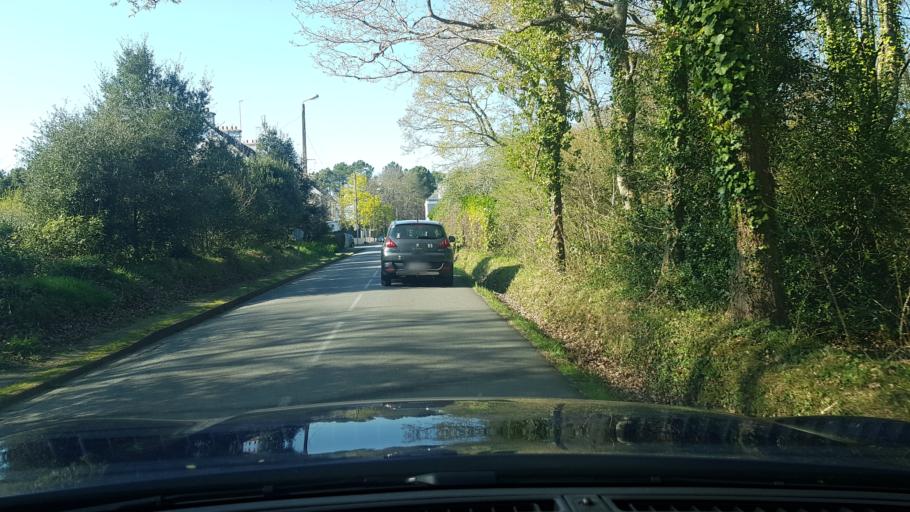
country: FR
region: Brittany
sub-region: Departement du Finistere
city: Moelan-sur-Mer
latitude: 47.8041
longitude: -3.6271
